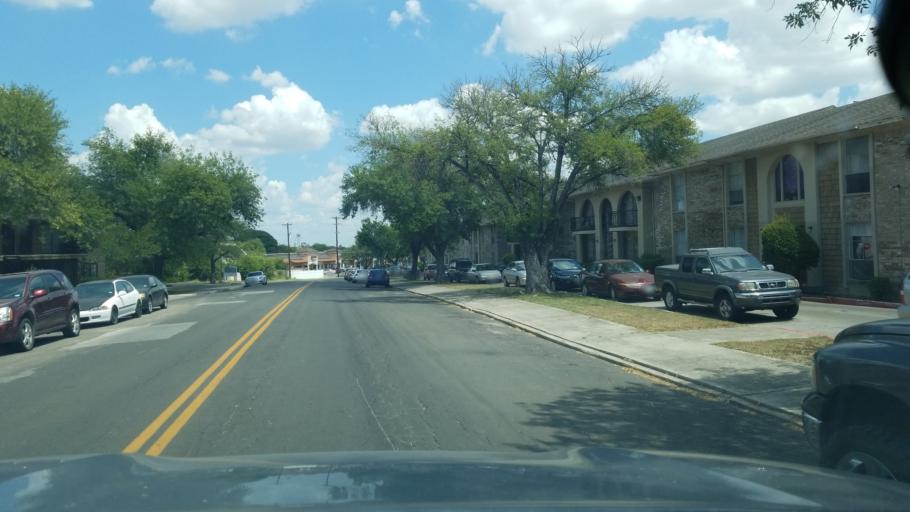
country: US
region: Texas
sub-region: Bexar County
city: Castle Hills
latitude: 29.5281
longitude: -98.5020
